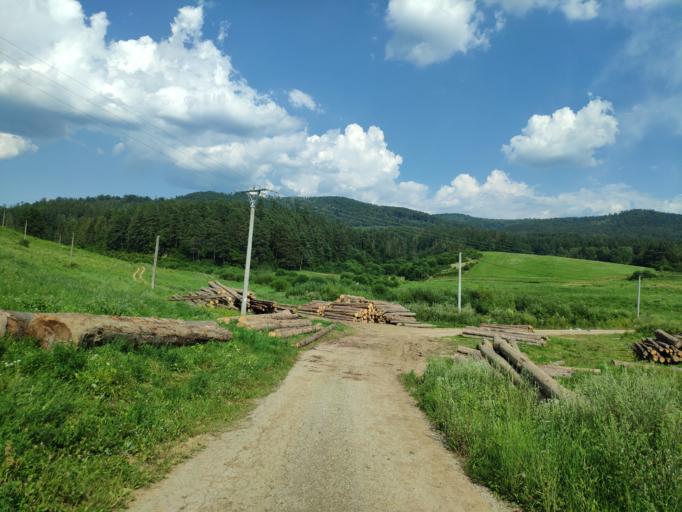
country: SK
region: Kosicky
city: Dobsina
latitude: 48.6958
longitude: 20.3533
